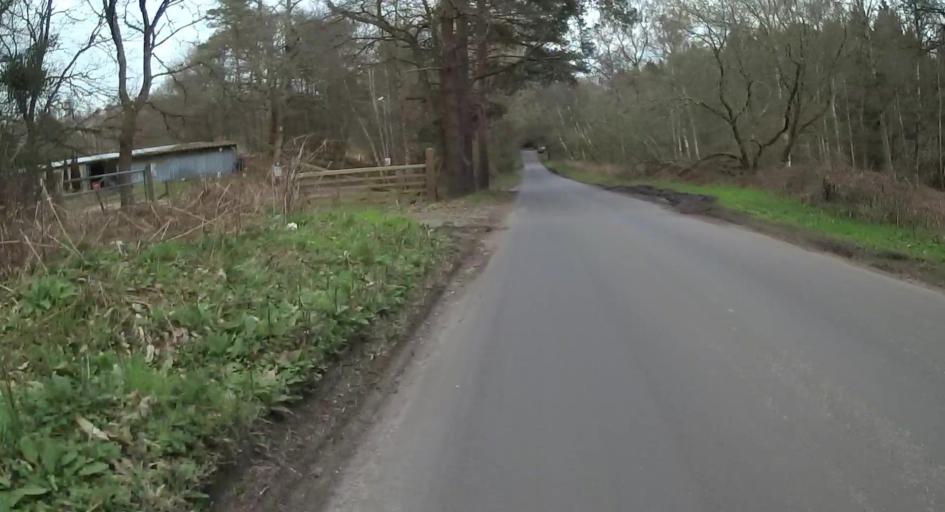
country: GB
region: England
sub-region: Hampshire
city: Lindford
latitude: 51.1394
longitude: -0.8411
